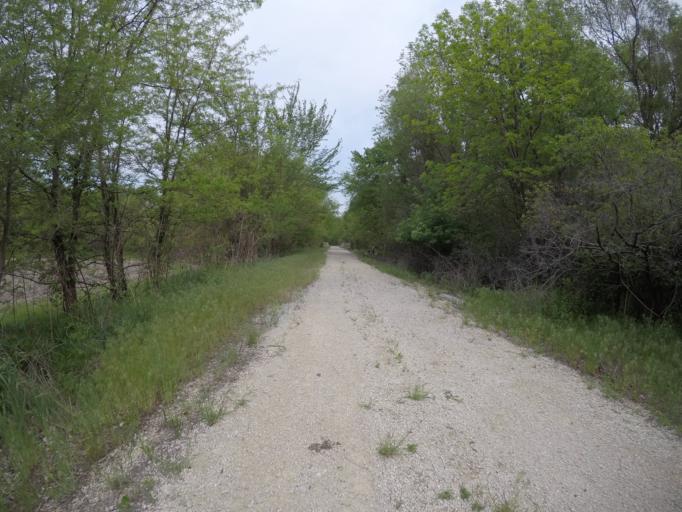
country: US
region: Nebraska
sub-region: Gage County
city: Beatrice
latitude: 40.2479
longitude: -96.6914
